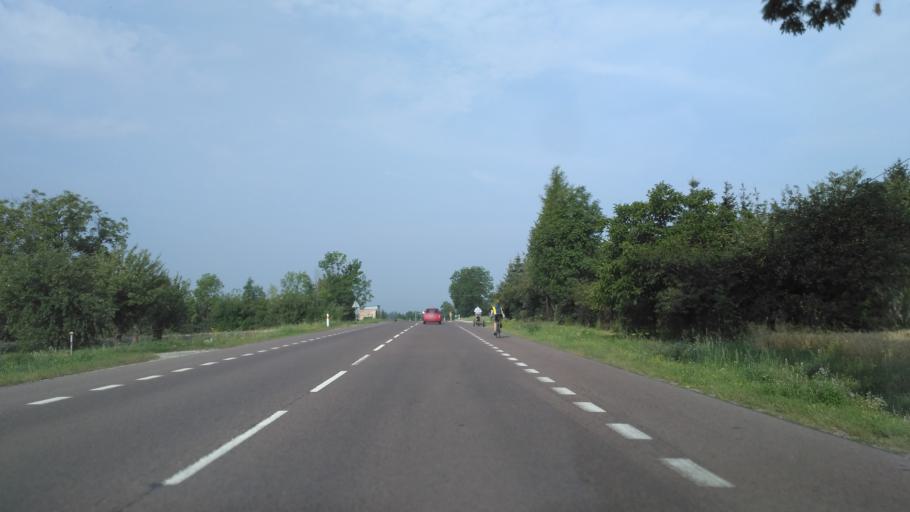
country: PL
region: Lublin Voivodeship
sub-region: Powiat swidnicki
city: Trawniki
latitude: 51.1673
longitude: 23.0772
